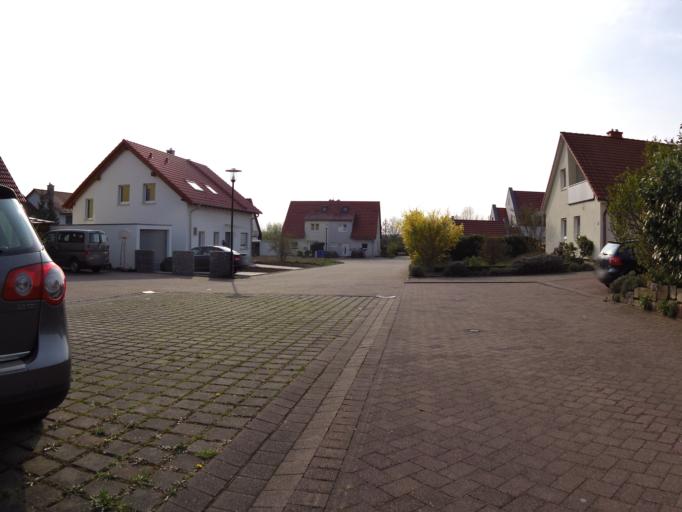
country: DE
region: Bavaria
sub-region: Regierungsbezirk Unterfranken
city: Rottendorf
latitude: 49.7905
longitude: 10.0176
